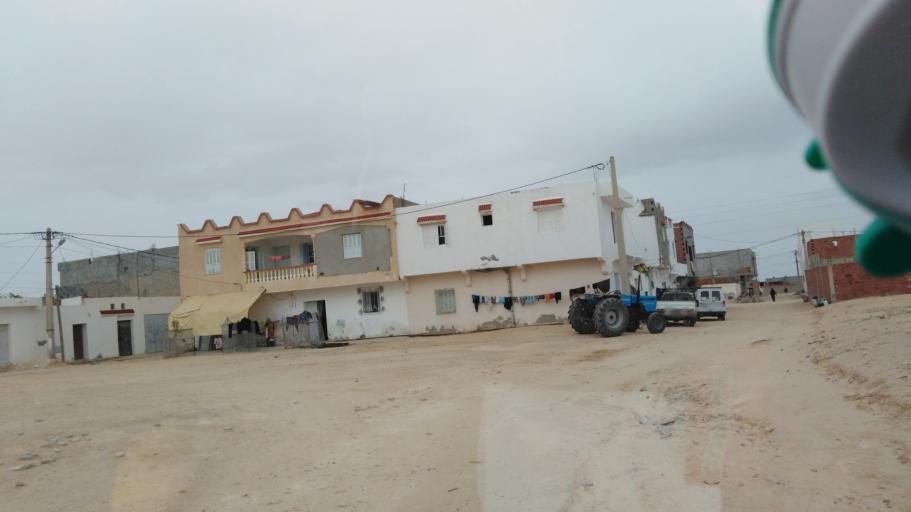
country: TN
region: Qabis
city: Gabes
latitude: 33.9511
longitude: 10.0036
